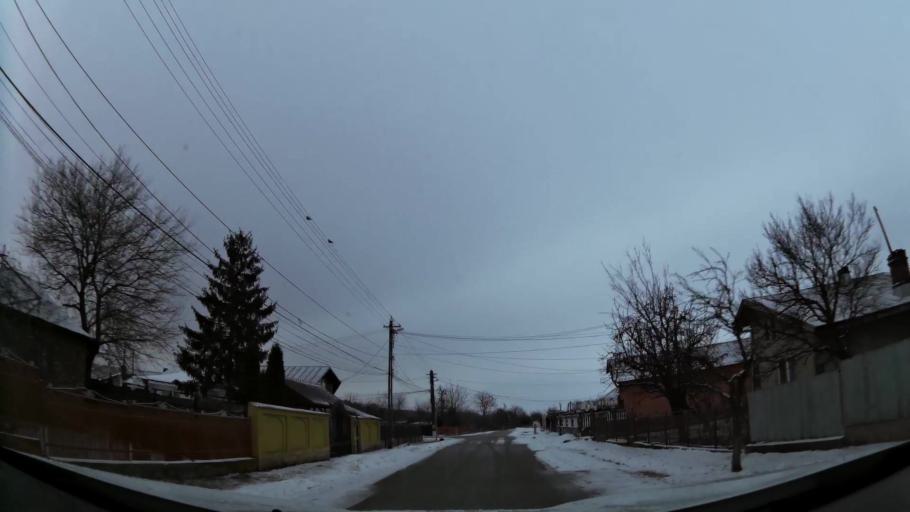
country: RO
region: Prahova
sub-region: Comuna Berceni
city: Corlatesti
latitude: 44.9098
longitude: 26.0907
